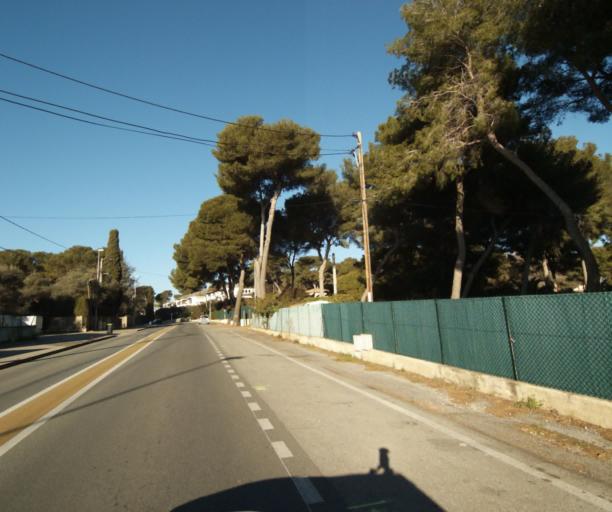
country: FR
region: Provence-Alpes-Cote d'Azur
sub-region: Departement des Alpes-Maritimes
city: Vallauris
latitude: 43.5960
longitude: 7.0808
